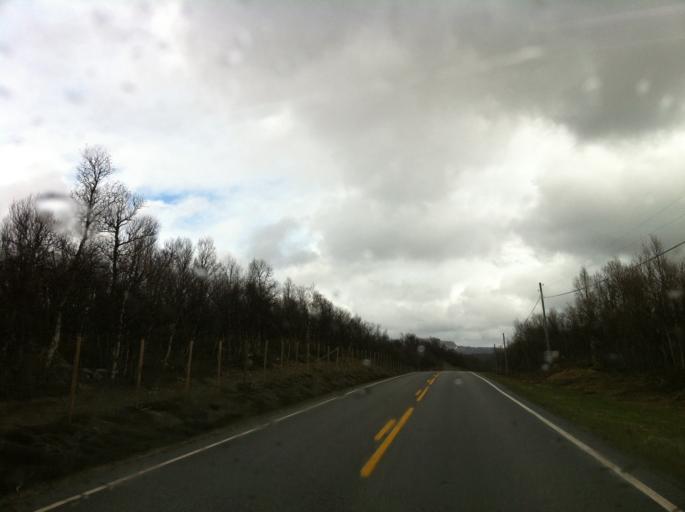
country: NO
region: Sor-Trondelag
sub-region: Tydal
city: Aas
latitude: 62.6449
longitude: 11.8803
